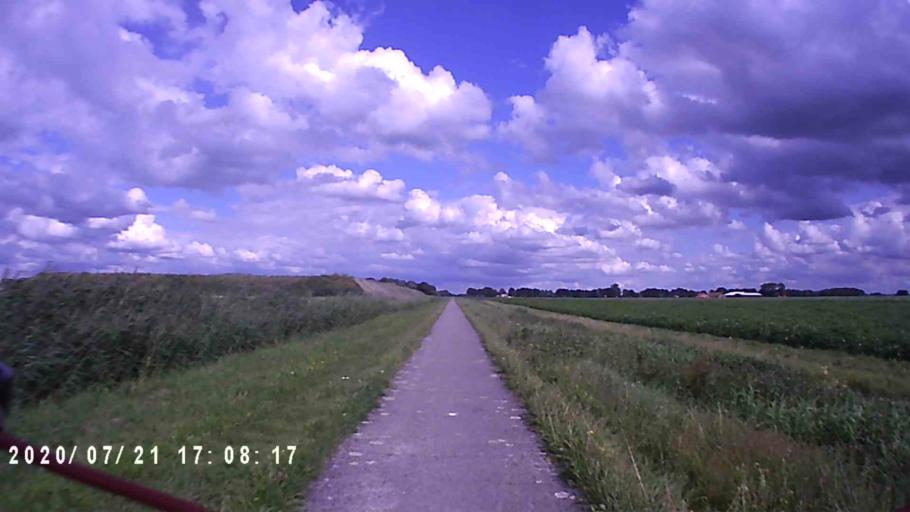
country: NL
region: Groningen
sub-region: Gemeente Hoogezand-Sappemeer
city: Hoogezand
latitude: 53.1300
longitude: 6.7454
